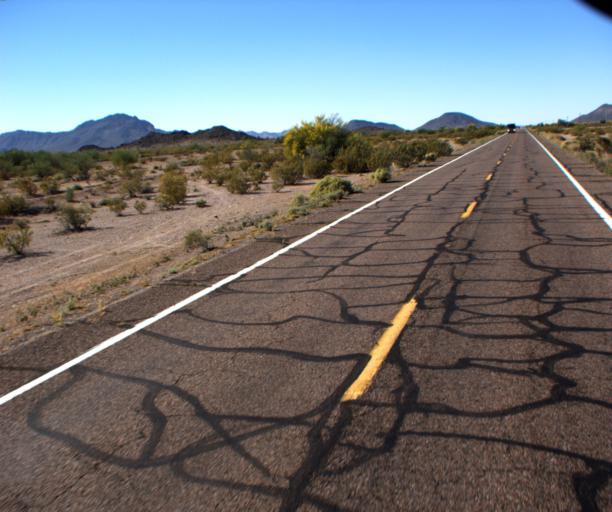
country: US
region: Arizona
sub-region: Maricopa County
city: Gila Bend
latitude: 32.8149
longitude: -112.7913
